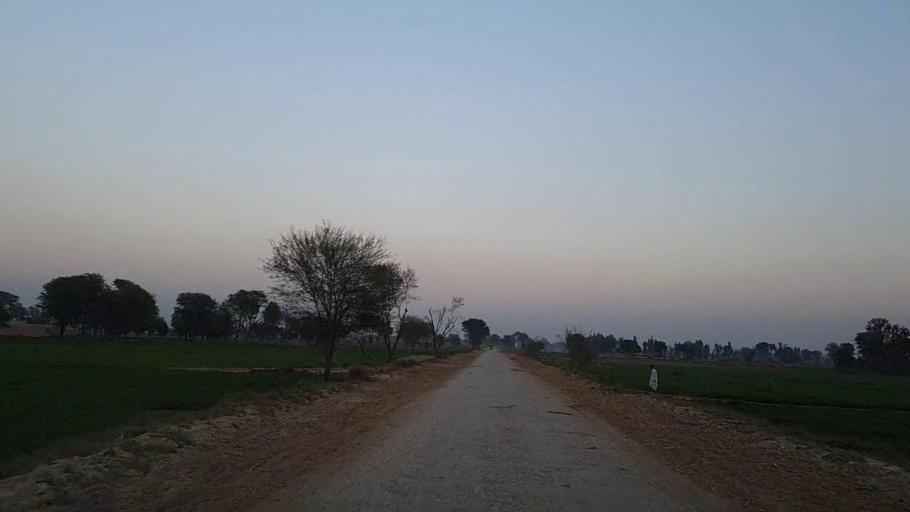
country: PK
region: Sindh
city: Naushahro Firoz
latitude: 26.8004
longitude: 68.0206
